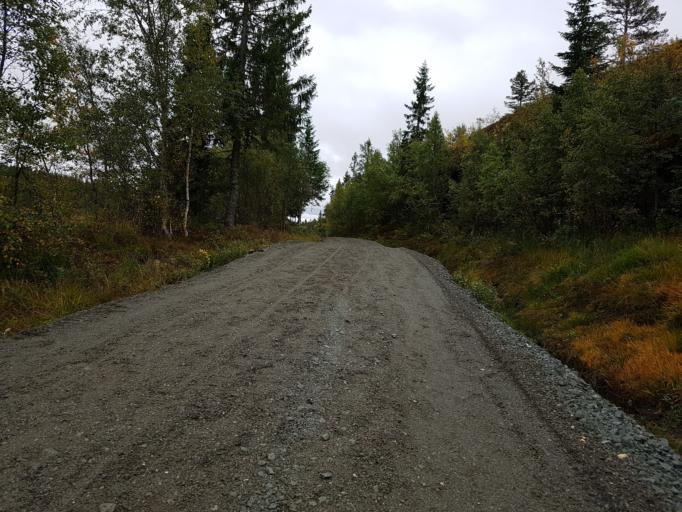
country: NO
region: Sor-Trondelag
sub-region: Melhus
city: Melhus
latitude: 63.4181
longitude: 10.2256
